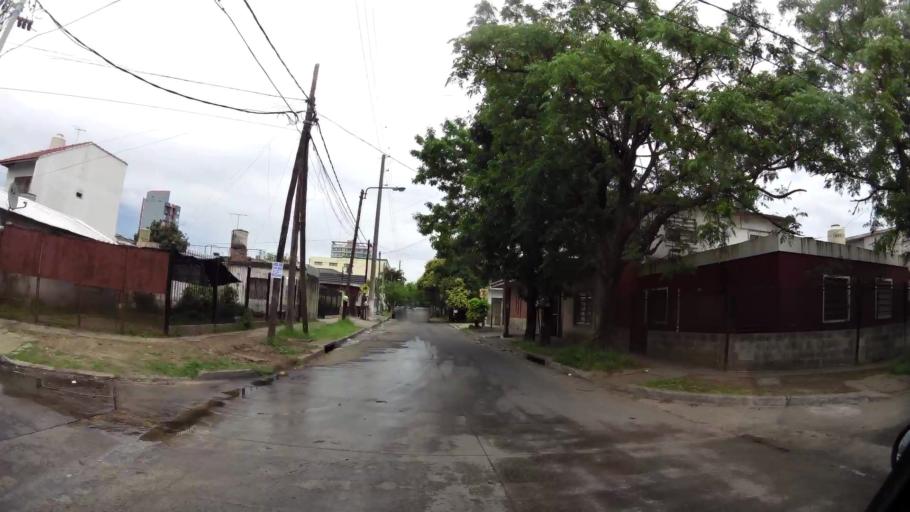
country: AR
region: Buenos Aires
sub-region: Partido de Quilmes
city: Quilmes
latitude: -34.7546
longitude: -58.2065
